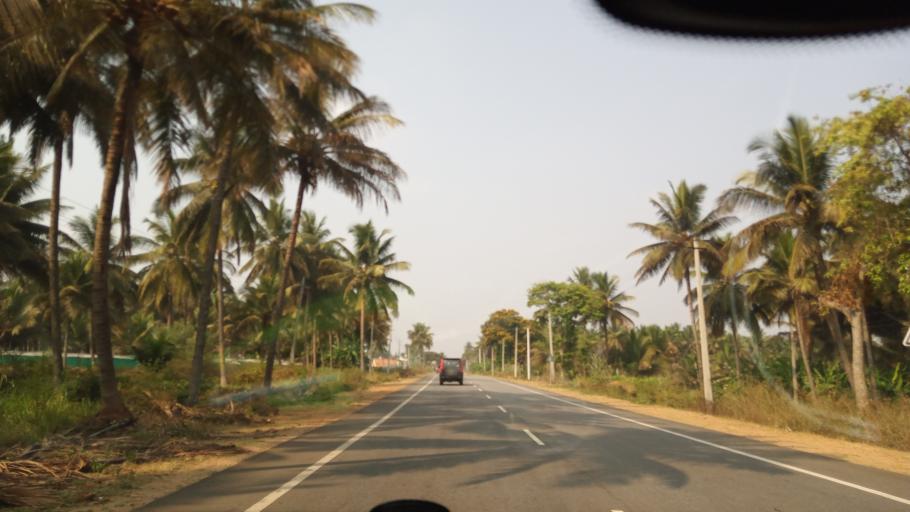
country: IN
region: Karnataka
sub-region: Mandya
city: Nagamangala
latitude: 12.7385
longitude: 76.7228
